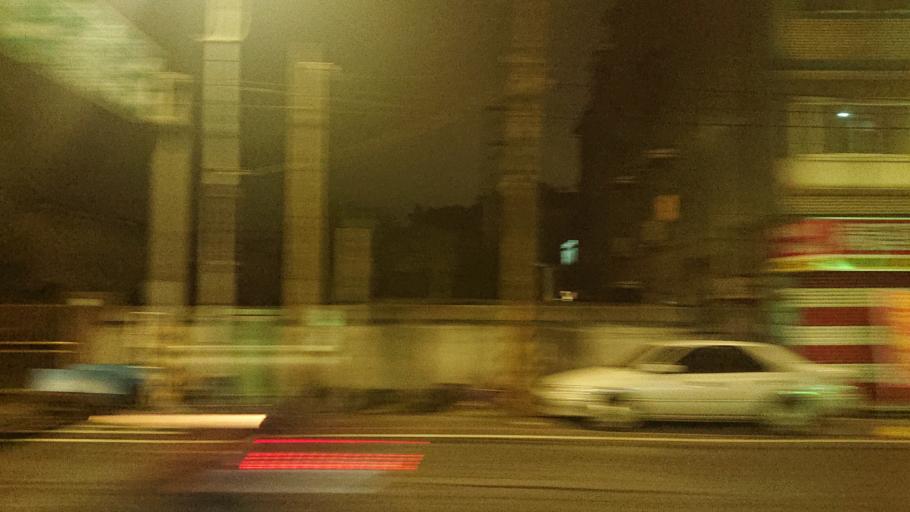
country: TW
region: Taiwan
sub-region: Taoyuan
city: Taoyuan
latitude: 24.9370
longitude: 121.3958
